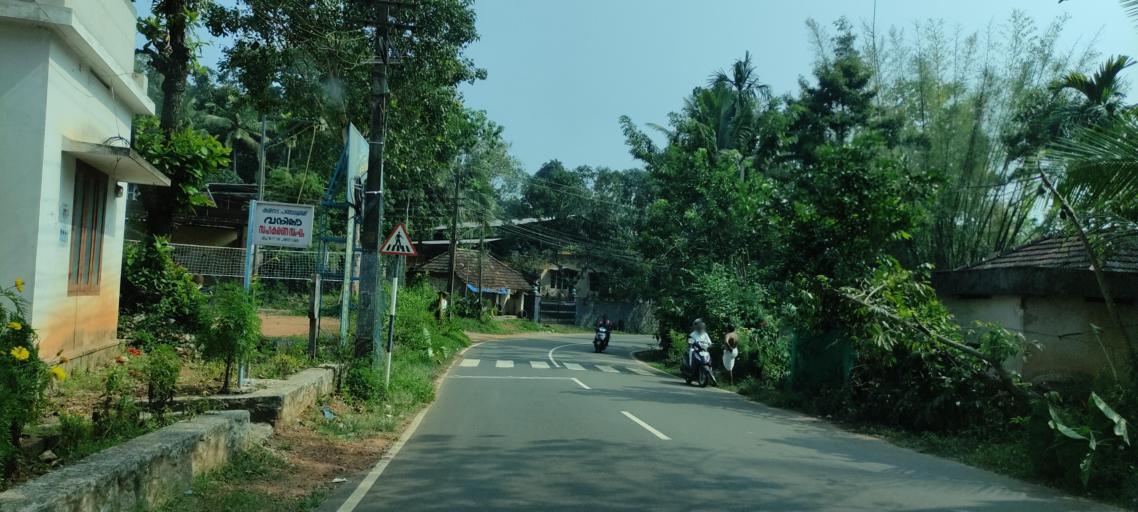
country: IN
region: Kerala
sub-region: Pattanamtitta
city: Adur
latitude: 9.2429
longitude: 76.6811
